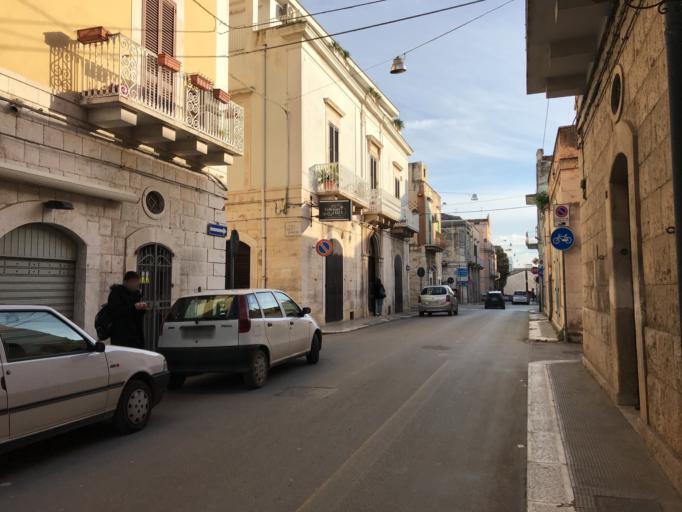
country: IT
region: Apulia
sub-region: Provincia di Bari
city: Corato
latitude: 41.1494
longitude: 16.4118
